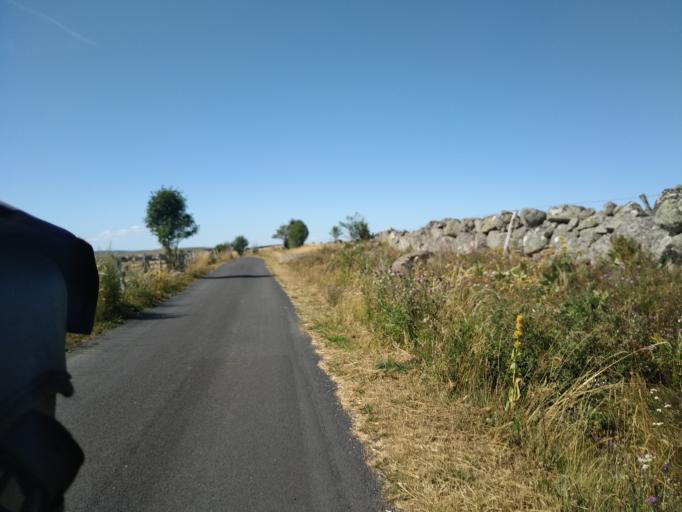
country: FR
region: Languedoc-Roussillon
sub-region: Departement de la Lozere
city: Aumont-Aubrac
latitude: 44.6757
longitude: 3.0979
